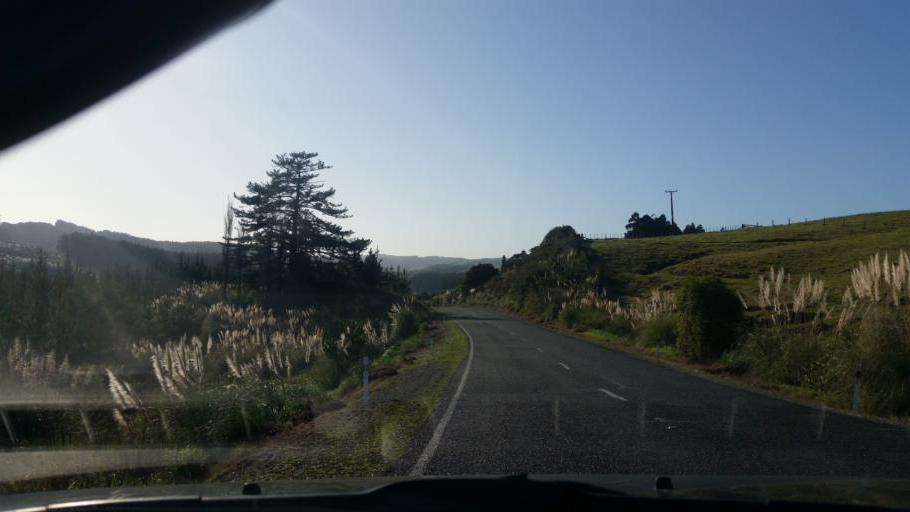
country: NZ
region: Auckland
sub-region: Auckland
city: Wellsford
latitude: -36.2232
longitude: 174.4564
